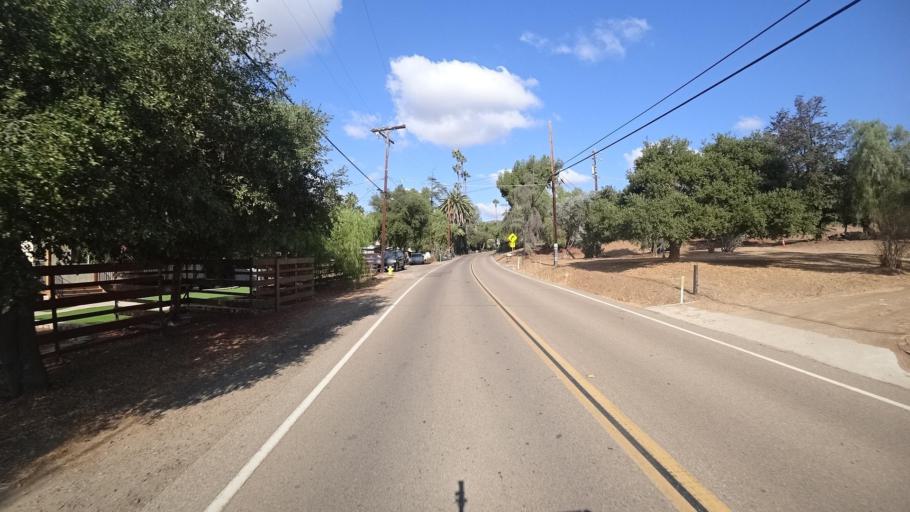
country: US
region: California
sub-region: San Diego County
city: Eucalyptus Hills
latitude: 32.8733
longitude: -116.9499
